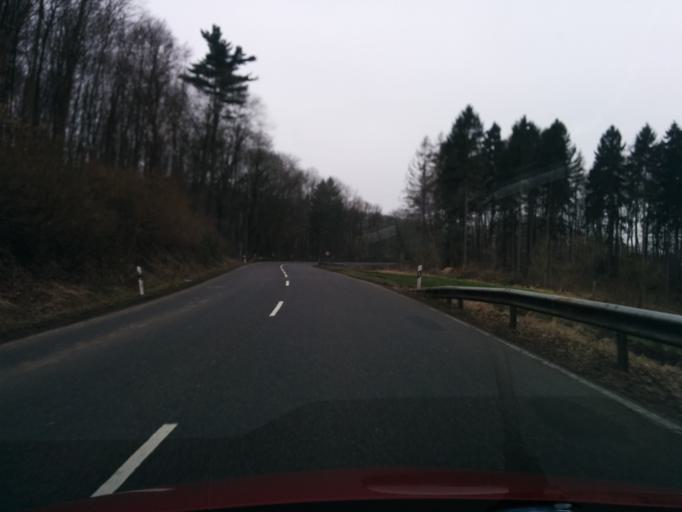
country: DE
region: Rheinland-Pfalz
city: Simmern
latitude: 50.3698
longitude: 7.6726
